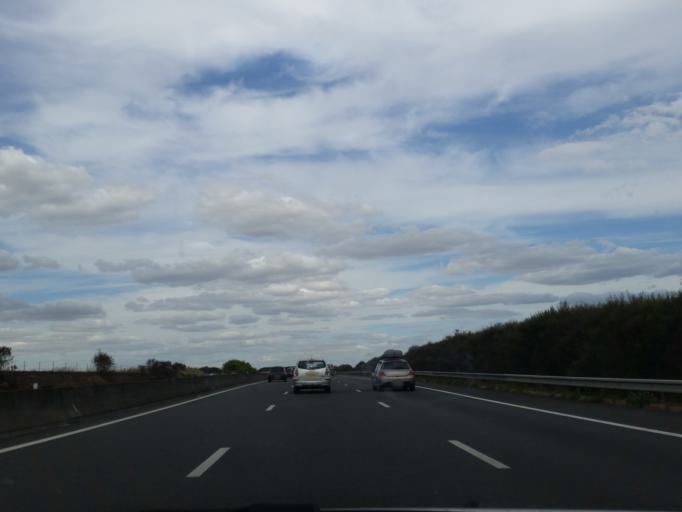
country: FR
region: Centre
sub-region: Departement d'Indre-et-Loire
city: Cangey
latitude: 47.5649
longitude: 1.0398
